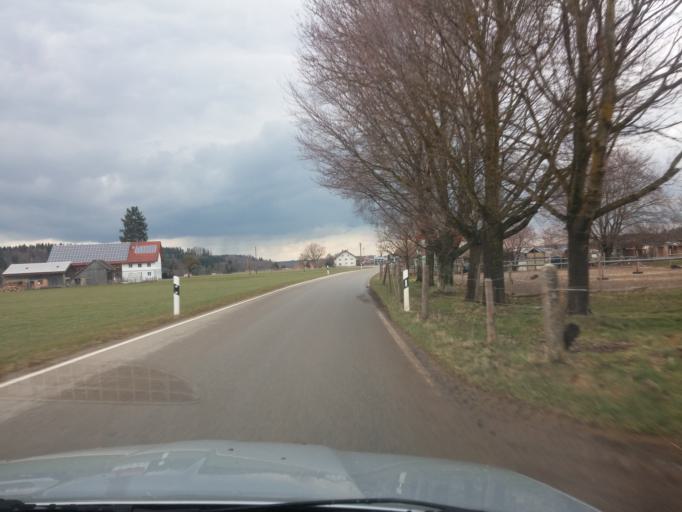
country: DE
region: Bavaria
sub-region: Swabia
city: Lautrach
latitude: 47.8873
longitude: 10.1121
